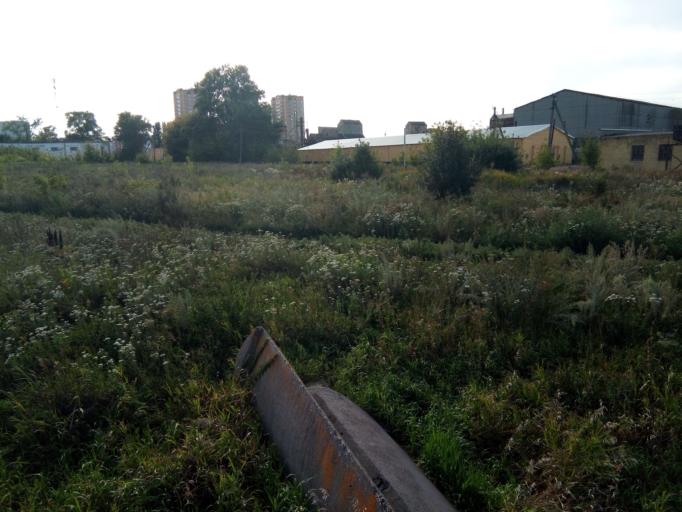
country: RU
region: Lipetsk
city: Lipetsk
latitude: 52.6353
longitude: 39.5517
